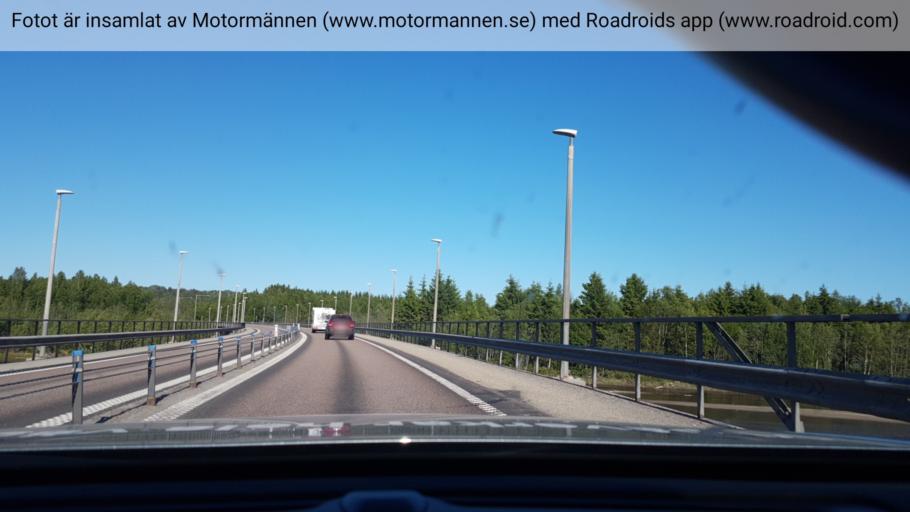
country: SE
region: Vaesternorrland
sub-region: Timra Kommun
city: Soraker
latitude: 62.5163
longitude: 17.4541
